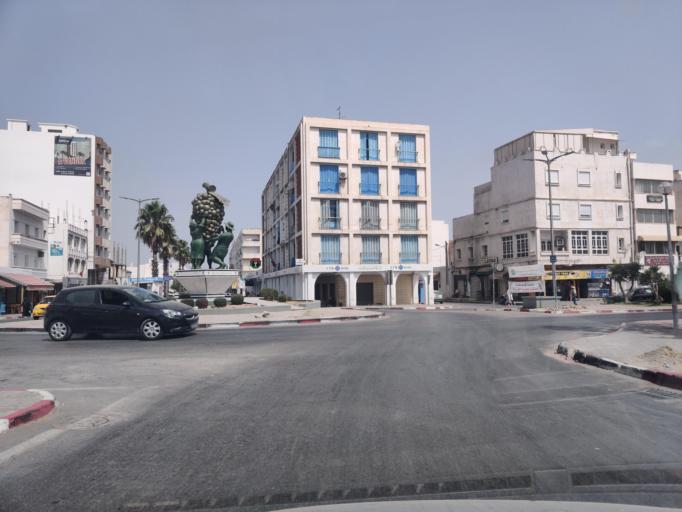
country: TN
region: Nabul
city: Bu `Urqub
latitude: 36.5982
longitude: 10.4992
